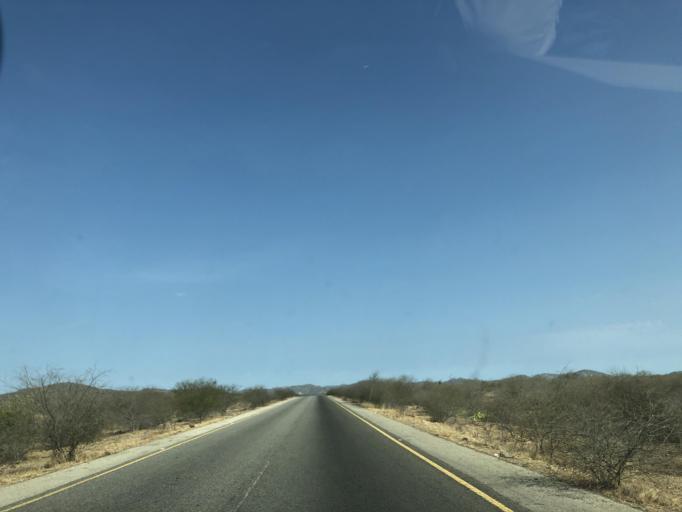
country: AO
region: Benguela
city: Benguela
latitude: -12.8790
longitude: 13.4446
